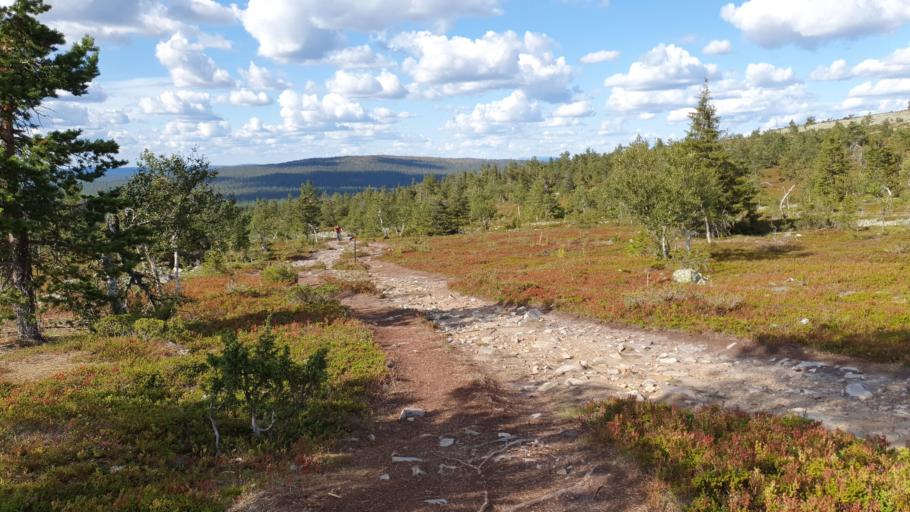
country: FI
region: Lapland
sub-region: Tunturi-Lappi
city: Kolari
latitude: 67.6139
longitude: 24.2601
